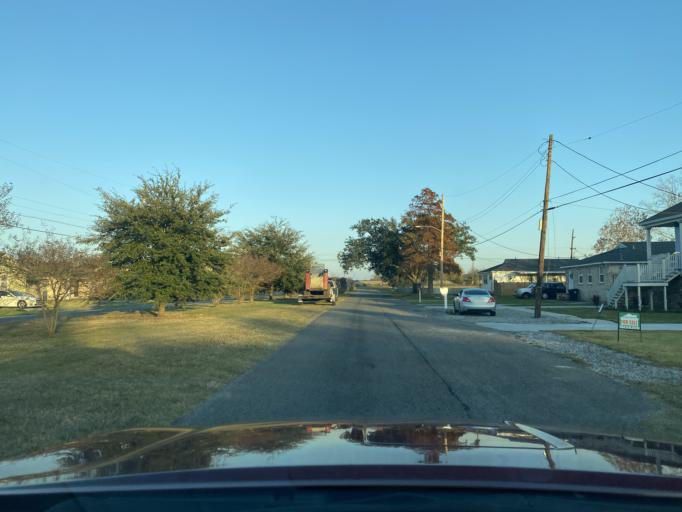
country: US
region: Louisiana
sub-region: Orleans Parish
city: New Orleans
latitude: 30.0226
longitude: -90.0494
